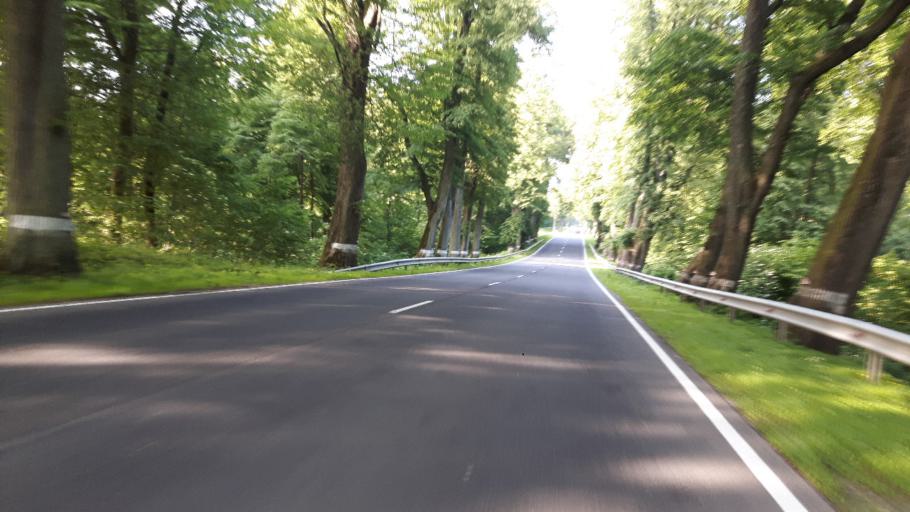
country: RU
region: Kaliningrad
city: Ladushkin
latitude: 54.5178
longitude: 20.1112
